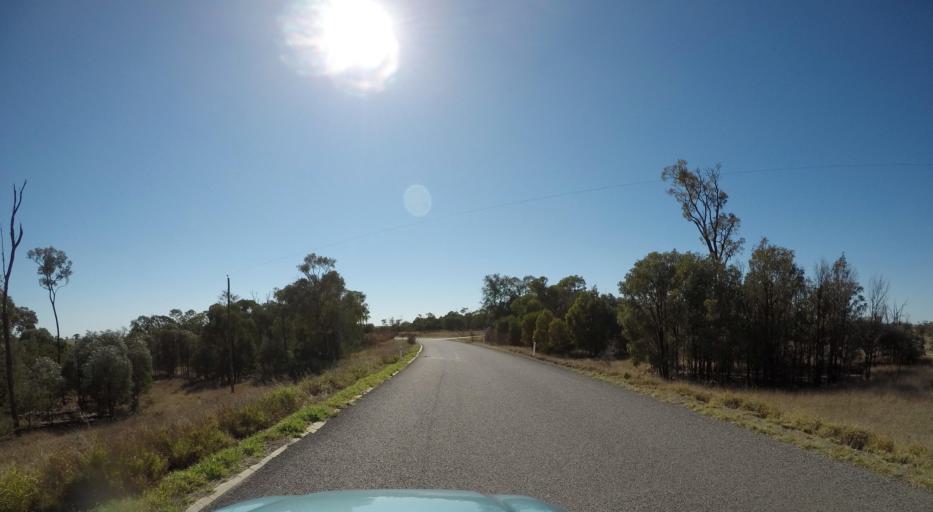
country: AU
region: Queensland
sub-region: Banana
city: Taroom
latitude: -25.7882
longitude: 149.6934
